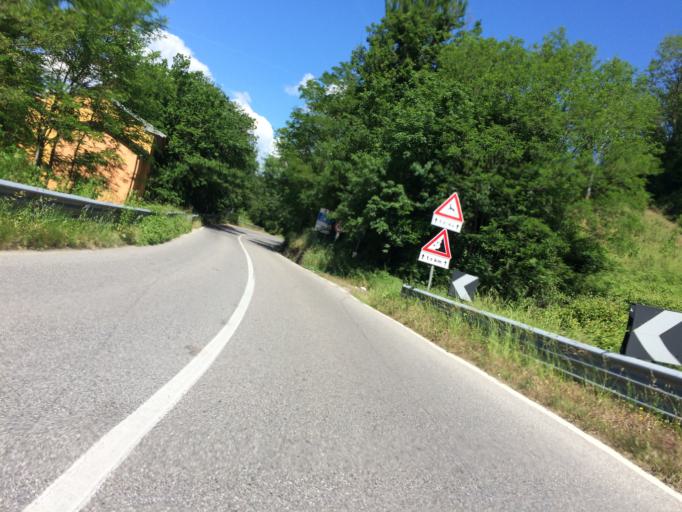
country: IT
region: Tuscany
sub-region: Provincia di Massa-Carrara
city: Terrarossa
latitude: 44.2464
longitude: 9.9602
